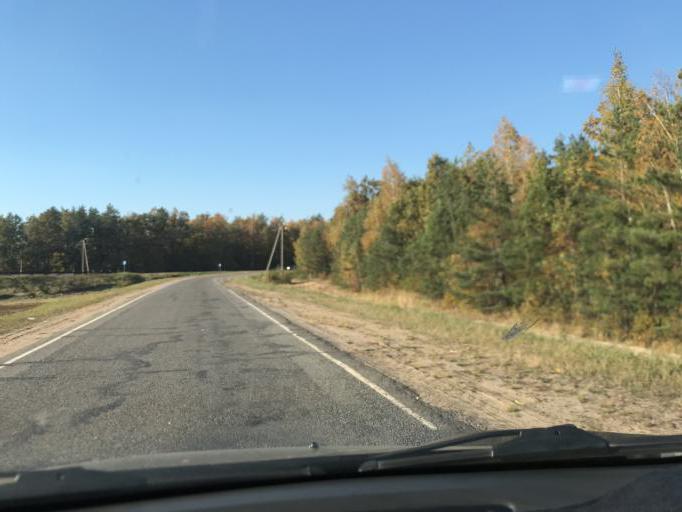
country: BY
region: Mogilev
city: Babruysk
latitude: 53.1072
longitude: 29.0582
